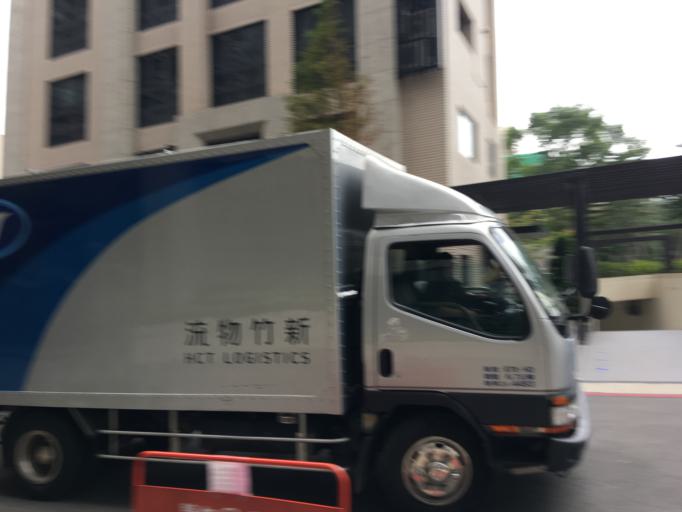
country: TW
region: Taiwan
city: Taoyuan City
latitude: 25.0175
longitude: 121.3055
